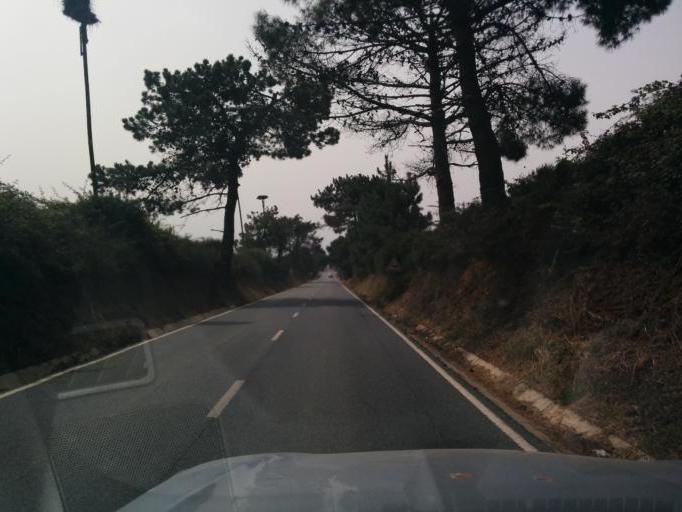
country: PT
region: Beja
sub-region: Odemira
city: Sao Teotonio
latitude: 37.5930
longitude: -8.7420
